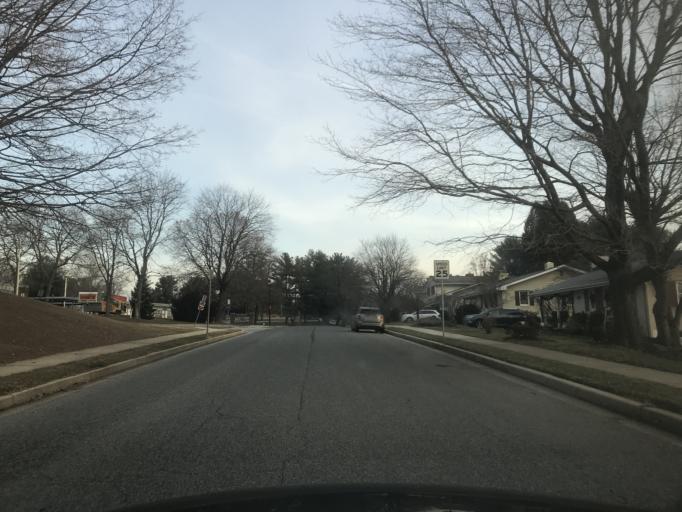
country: US
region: Maryland
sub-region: Baltimore County
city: Timonium
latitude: 39.4536
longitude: -76.6138
